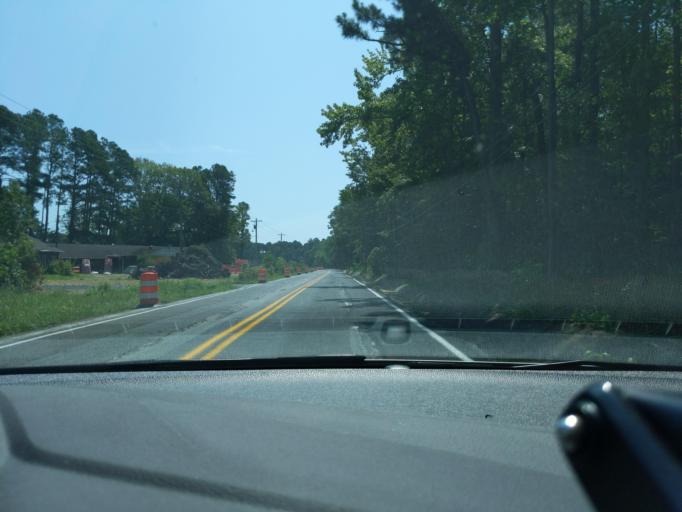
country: US
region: Virginia
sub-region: Northumberland County
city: Heathsville
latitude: 38.0762
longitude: -76.3475
